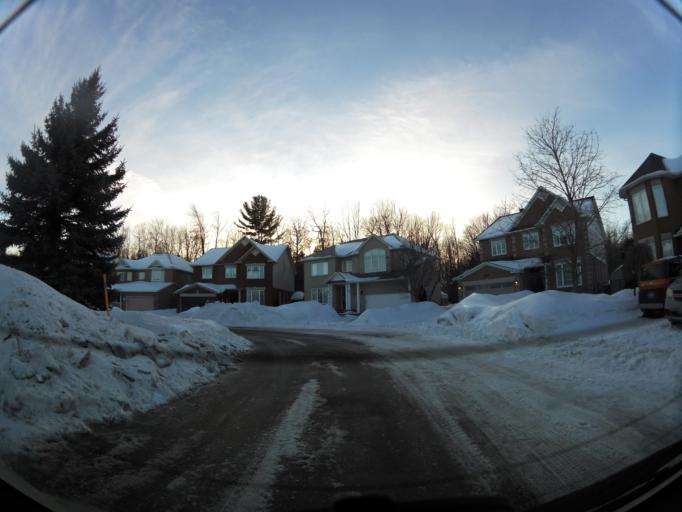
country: CA
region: Ontario
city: Ottawa
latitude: 45.4389
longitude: -75.5331
